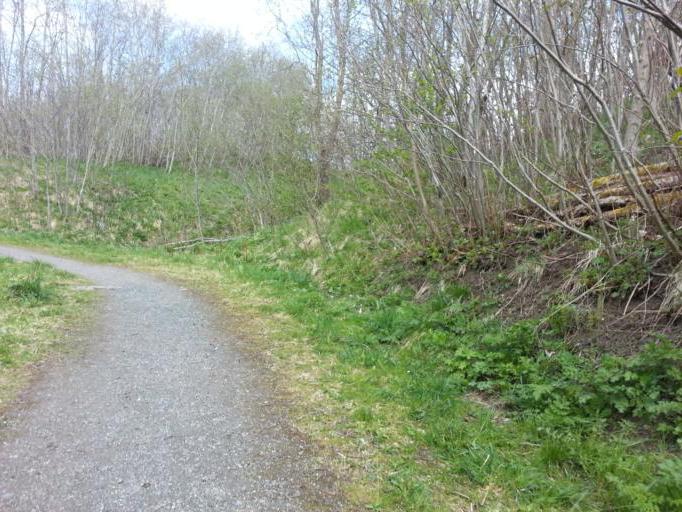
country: NO
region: Sor-Trondelag
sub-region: Trondheim
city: Trondheim
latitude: 63.3906
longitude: 10.3585
